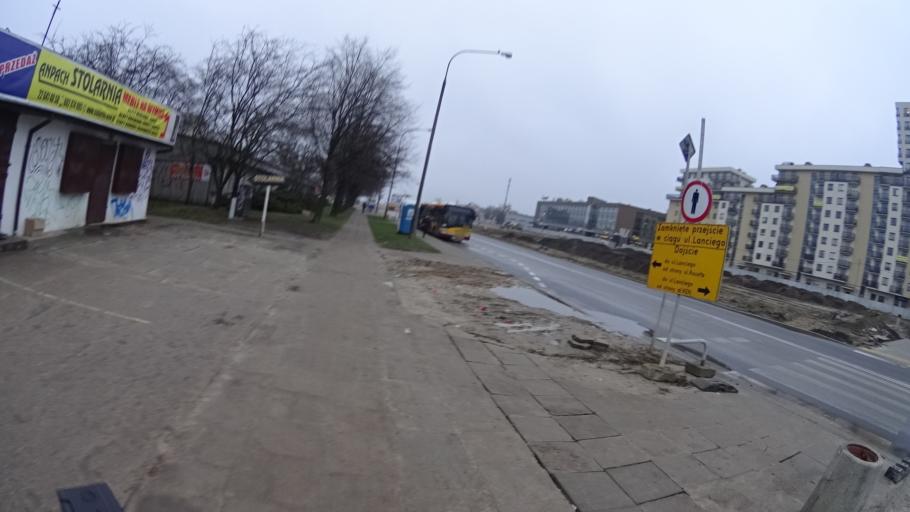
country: PL
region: Masovian Voivodeship
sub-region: Warszawa
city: Ursynow
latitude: 52.1469
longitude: 21.0559
